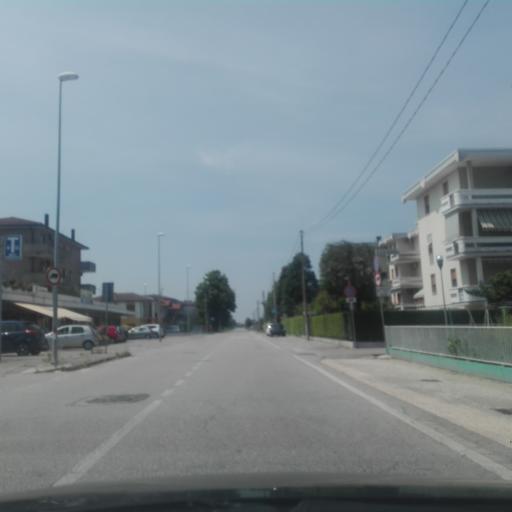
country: IT
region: Veneto
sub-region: Provincia di Rovigo
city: Adria
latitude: 45.0582
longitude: 12.0463
